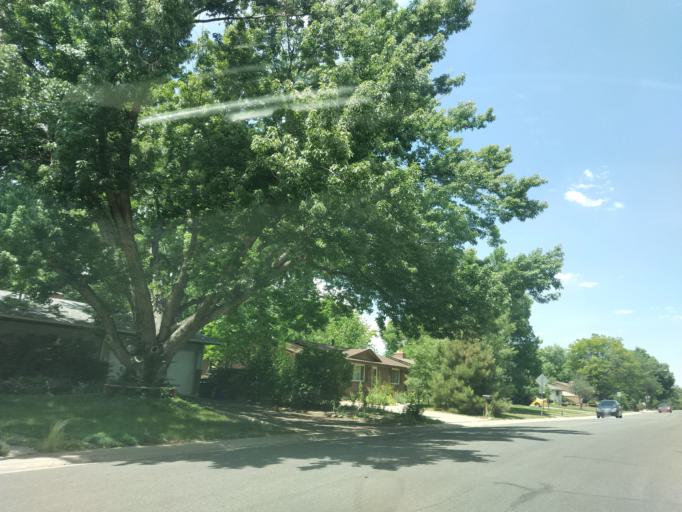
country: US
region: Colorado
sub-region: Jefferson County
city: Lakewood
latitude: 39.6789
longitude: -105.0908
